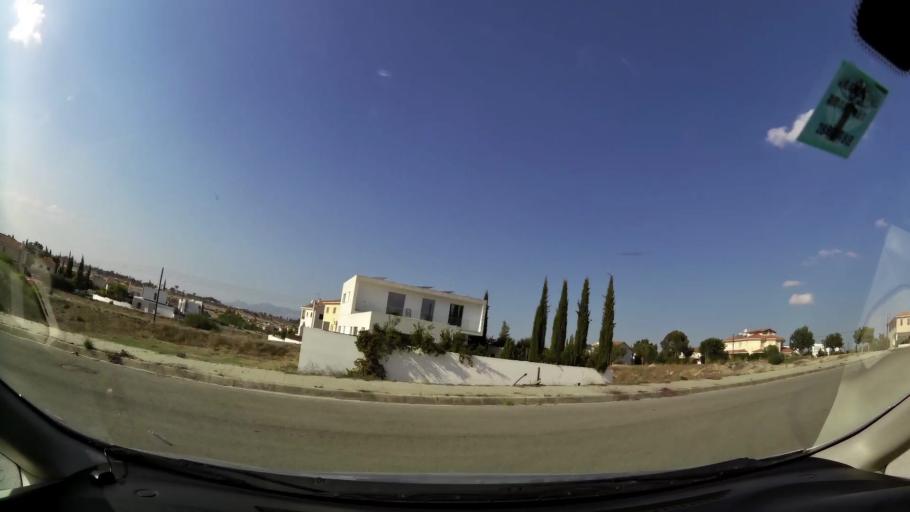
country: CY
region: Lefkosia
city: Kato Deftera
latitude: 35.1432
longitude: 33.3008
